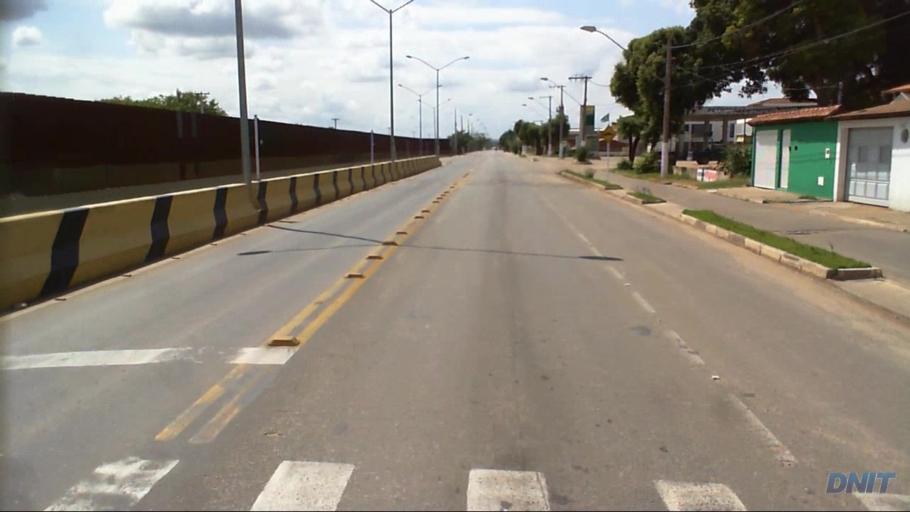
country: BR
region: Minas Gerais
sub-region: Governador Valadares
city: Governador Valadares
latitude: -18.9039
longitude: -41.9888
